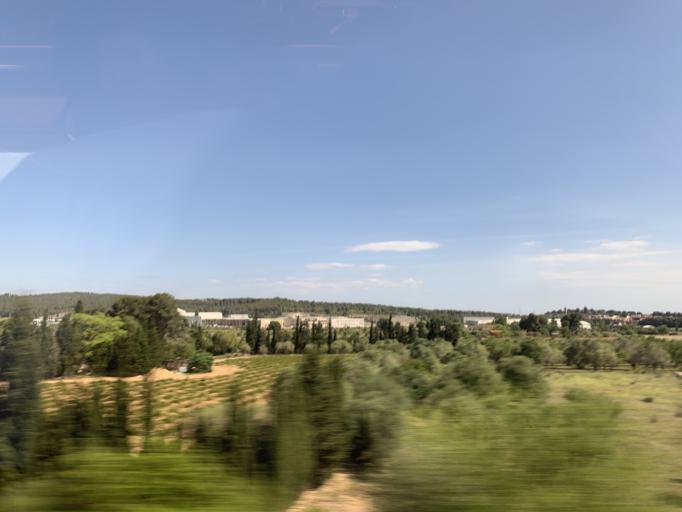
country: ES
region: Catalonia
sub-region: Provincia de Tarragona
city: Santa Oliva
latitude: 41.2341
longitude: 1.5455
